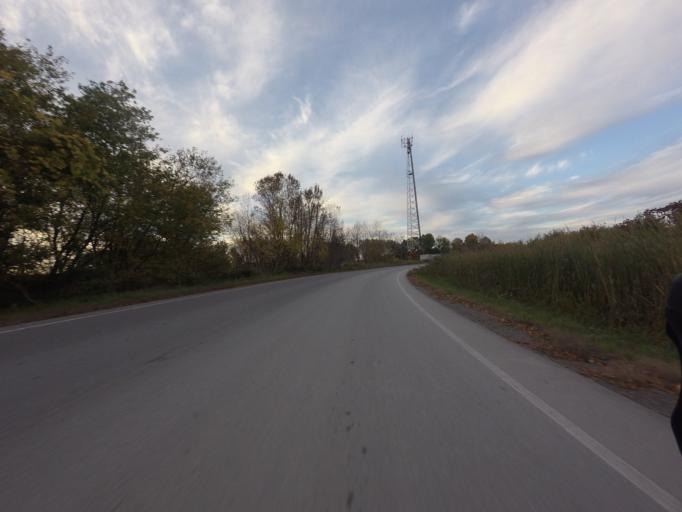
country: CA
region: Ontario
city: Oshawa
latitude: 43.8989
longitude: -78.6535
